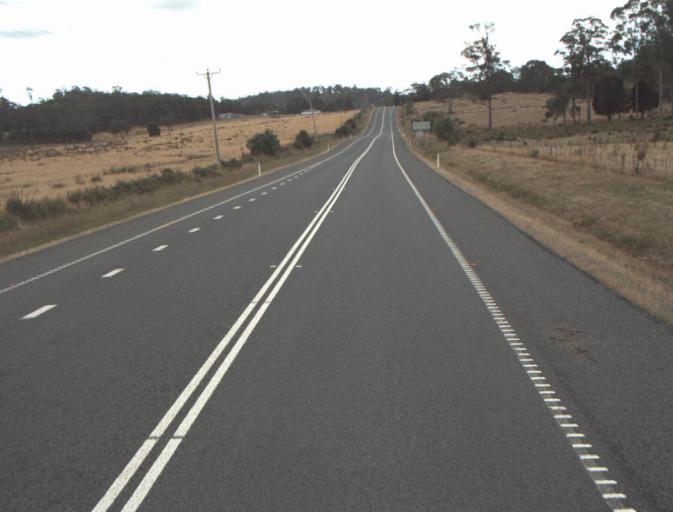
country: AU
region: Tasmania
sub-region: Launceston
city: Mayfield
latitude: -41.2550
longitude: 147.0242
